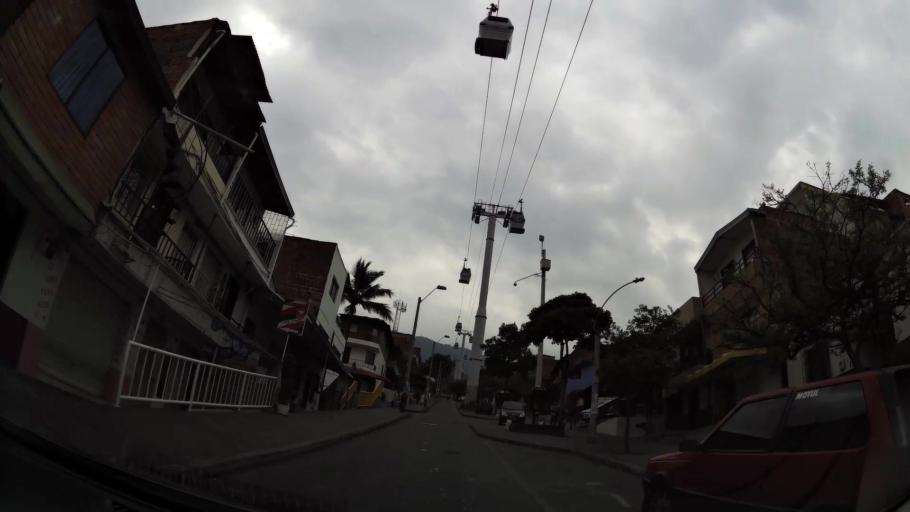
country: CO
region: Antioquia
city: Bello
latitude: 6.2991
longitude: -75.5565
